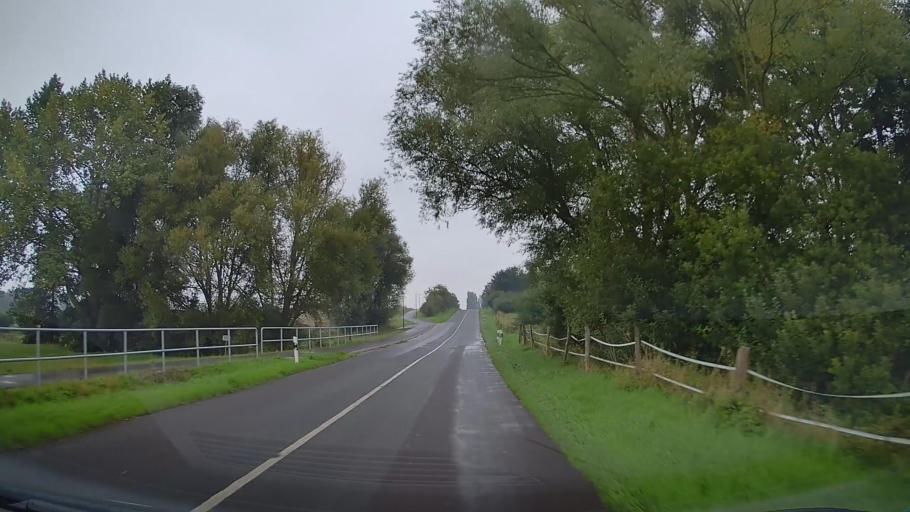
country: DE
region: Mecklenburg-Vorpommern
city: Gramkow
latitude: 53.9234
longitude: 11.3170
